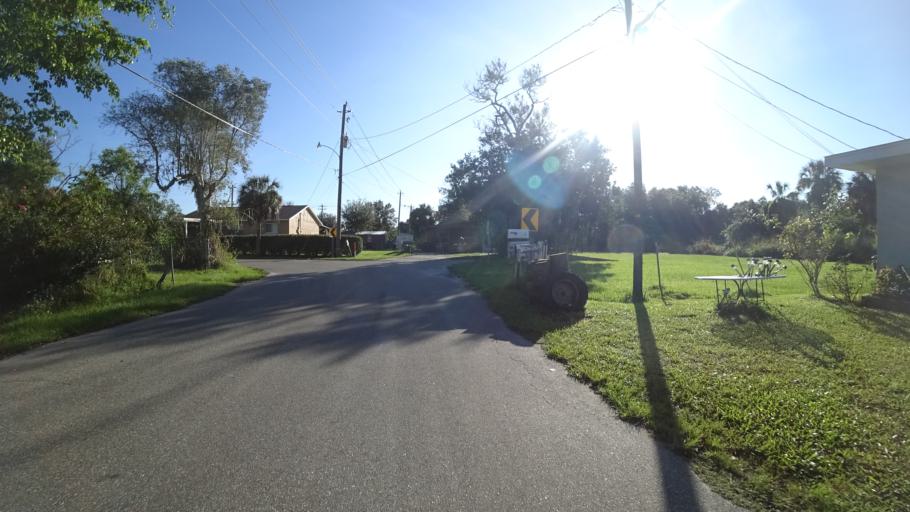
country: US
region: Florida
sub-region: Manatee County
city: Memphis
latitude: 27.5789
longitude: -82.5486
